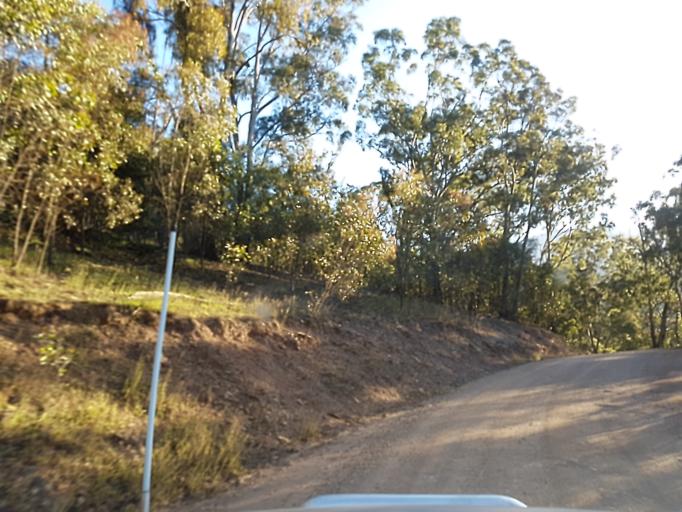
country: AU
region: Victoria
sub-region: Wellington
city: Heyfield
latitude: -37.4039
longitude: 147.0960
